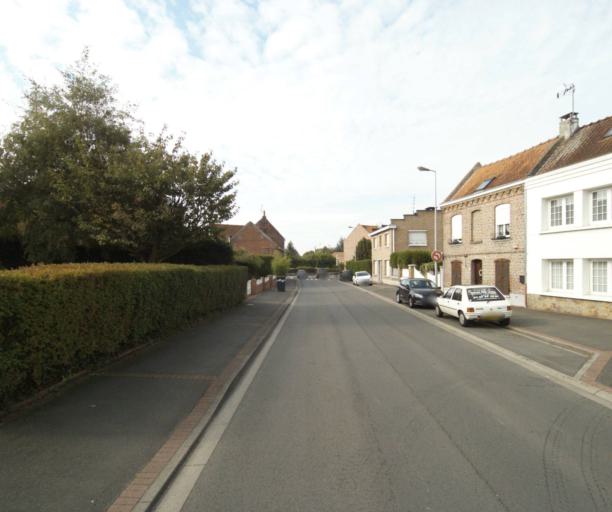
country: FR
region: Nord-Pas-de-Calais
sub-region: Departement du Nord
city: Wattignies
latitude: 50.5831
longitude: 3.0381
